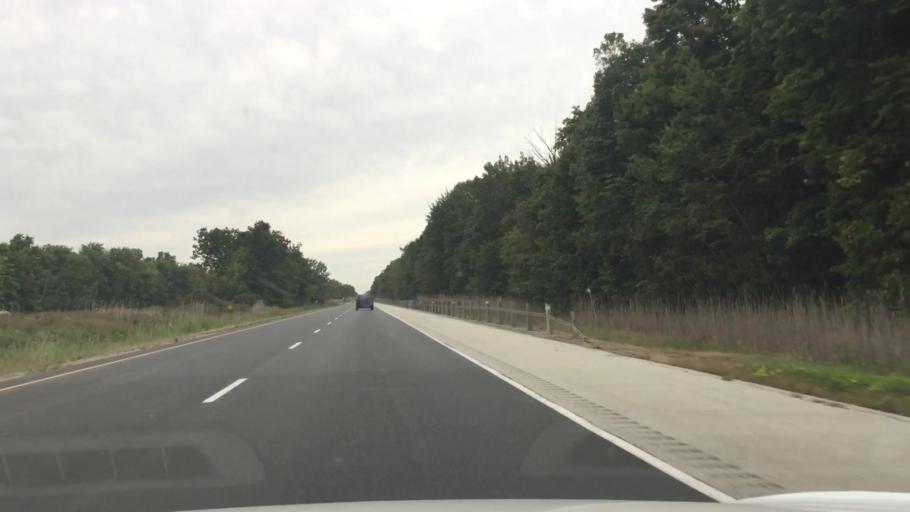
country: CA
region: Ontario
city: Camlachie
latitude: 42.9914
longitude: -82.0214
